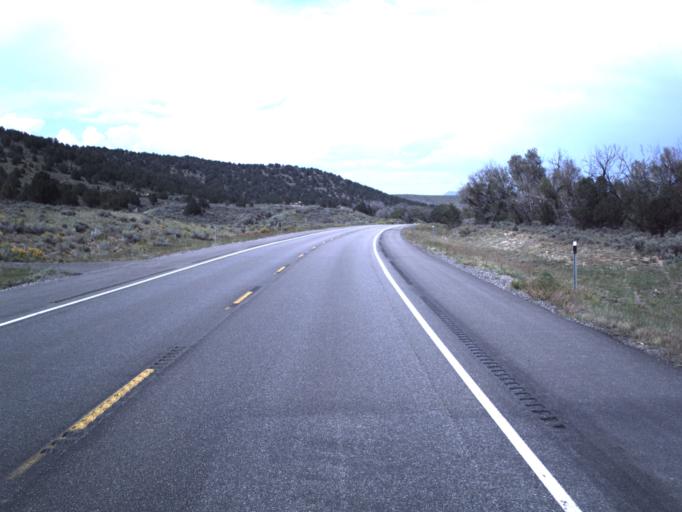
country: US
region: Utah
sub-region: Garfield County
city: Panguitch
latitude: 37.7929
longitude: -112.3966
